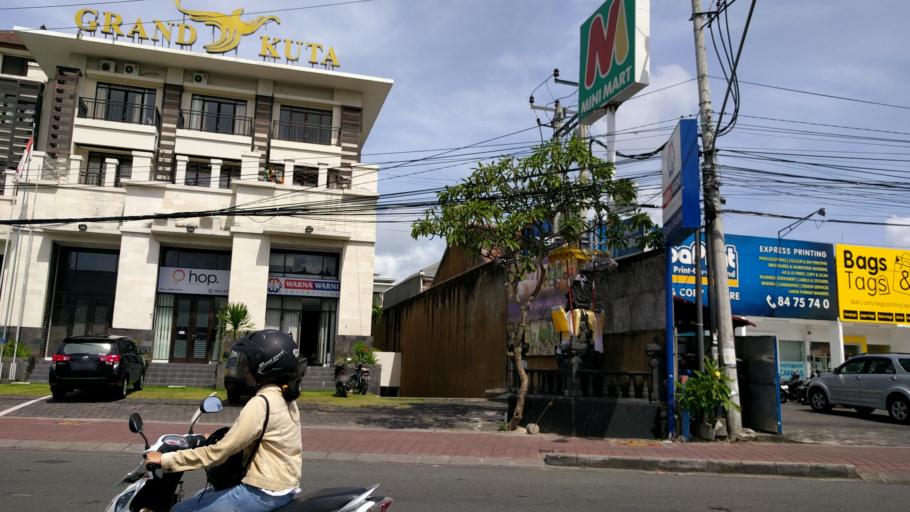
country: ID
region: Bali
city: Kuta
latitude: -8.7003
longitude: 115.1774
